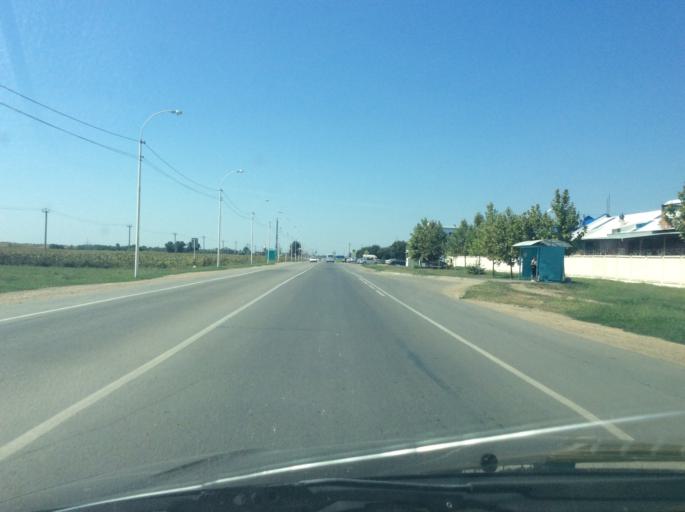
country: RU
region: Krasnodarskiy
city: Slavyansk-na-Kubani
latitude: 45.2489
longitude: 38.0901
